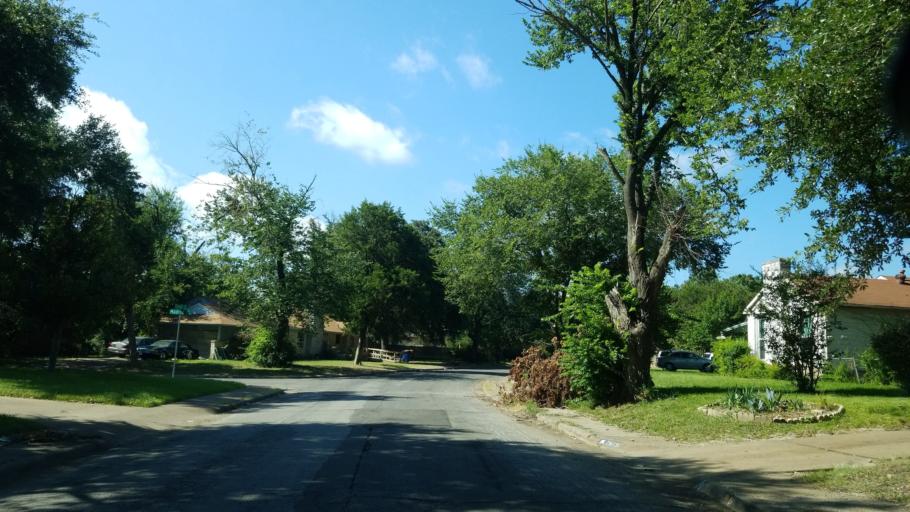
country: US
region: Texas
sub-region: Dallas County
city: Dallas
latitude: 32.7165
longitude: -96.8032
